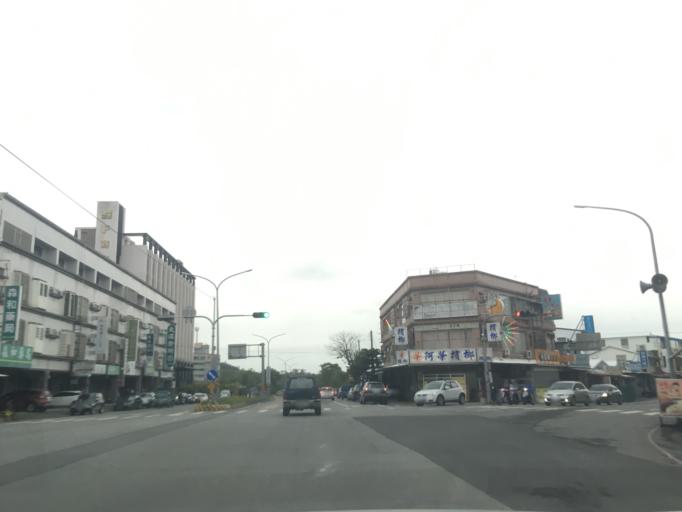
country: TW
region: Taiwan
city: Taitung City
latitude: 22.7064
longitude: 121.0419
